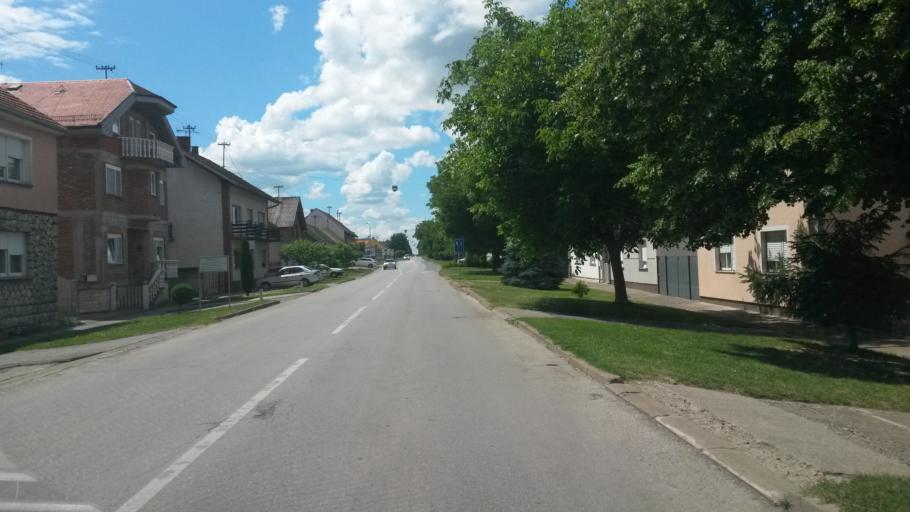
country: HR
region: Osjecko-Baranjska
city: Piskorevci
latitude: 45.3105
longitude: 18.3999
